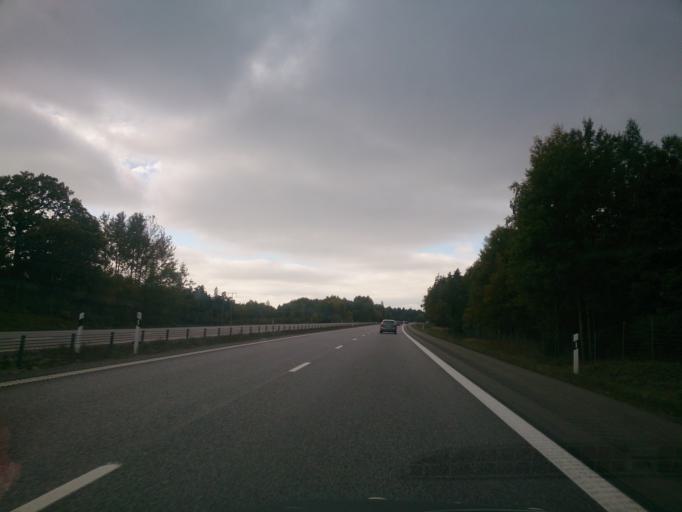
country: SE
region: OEstergoetland
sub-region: Linkopings Kommun
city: Linghem
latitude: 58.4586
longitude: 15.7849
